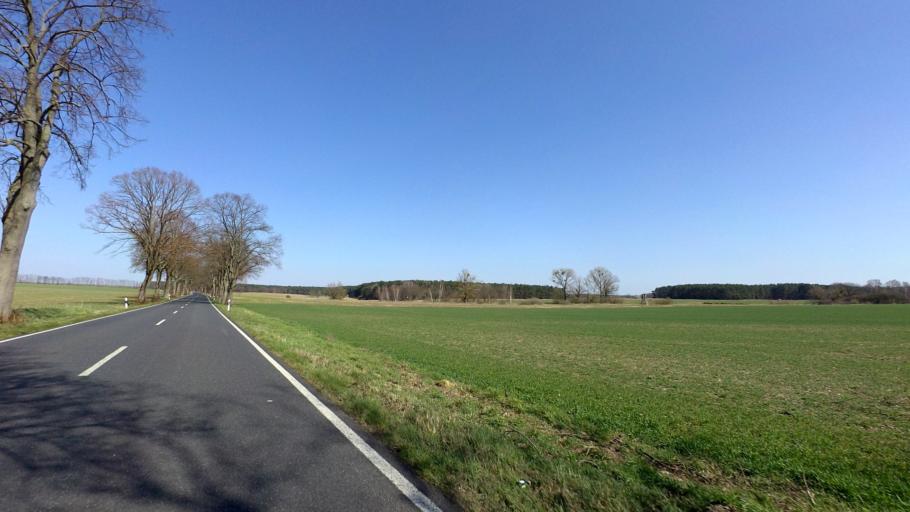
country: DE
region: Brandenburg
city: Sonnenberg
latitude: 52.9885
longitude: 13.0524
